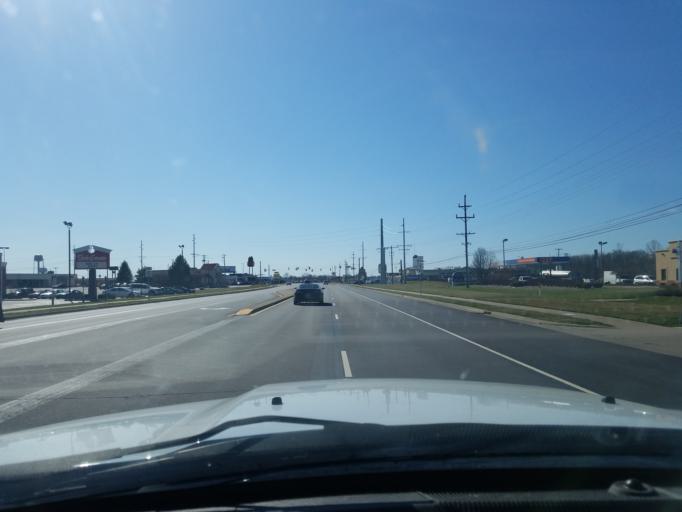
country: US
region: Indiana
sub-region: Shelby County
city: Shelbyville
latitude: 39.5246
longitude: -85.7405
